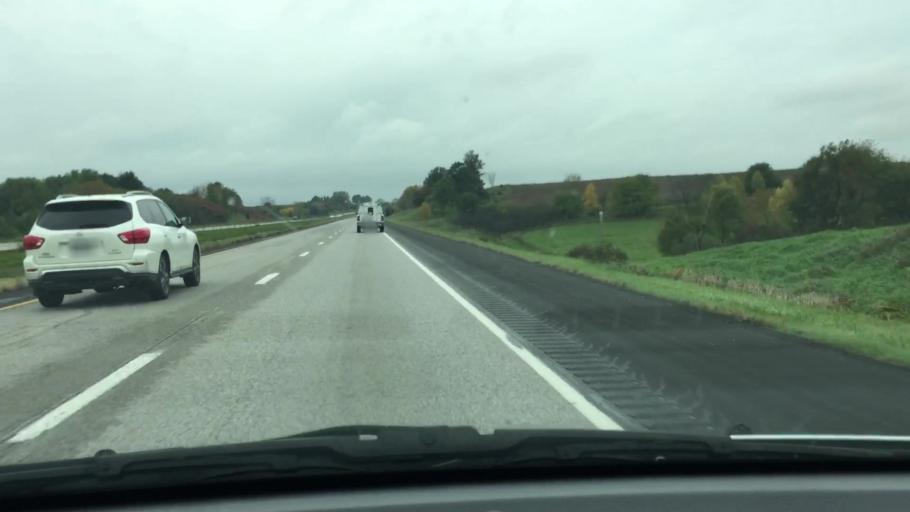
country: US
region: Iowa
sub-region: Johnson County
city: Tiffin
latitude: 41.6899
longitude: -91.7672
